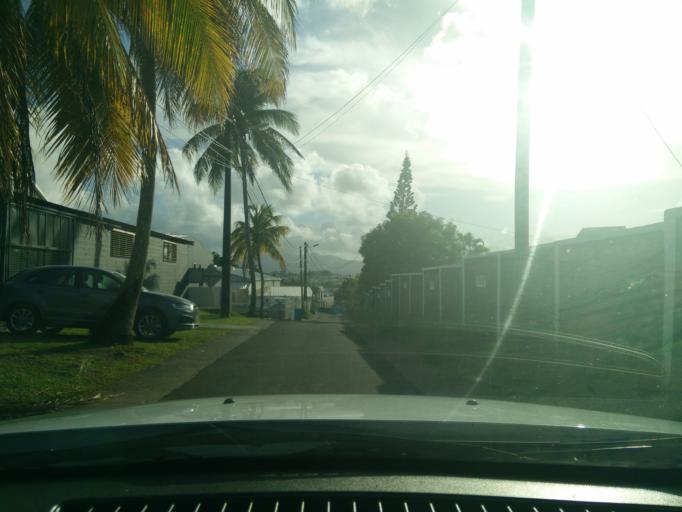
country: GP
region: Guadeloupe
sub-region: Guadeloupe
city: Baie-Mahault
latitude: 16.2526
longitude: -61.5857
